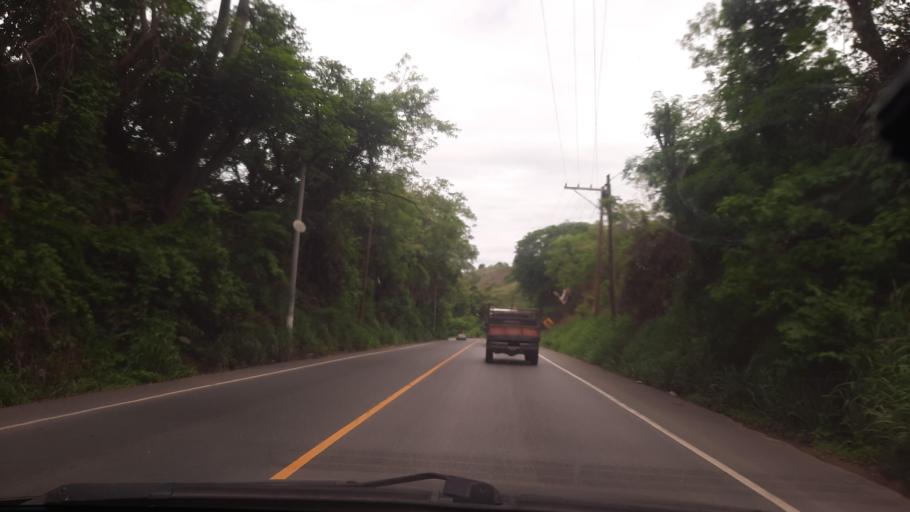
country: GT
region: Zacapa
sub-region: Municipio de Zacapa
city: Gualan
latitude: 15.1393
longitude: -89.3376
